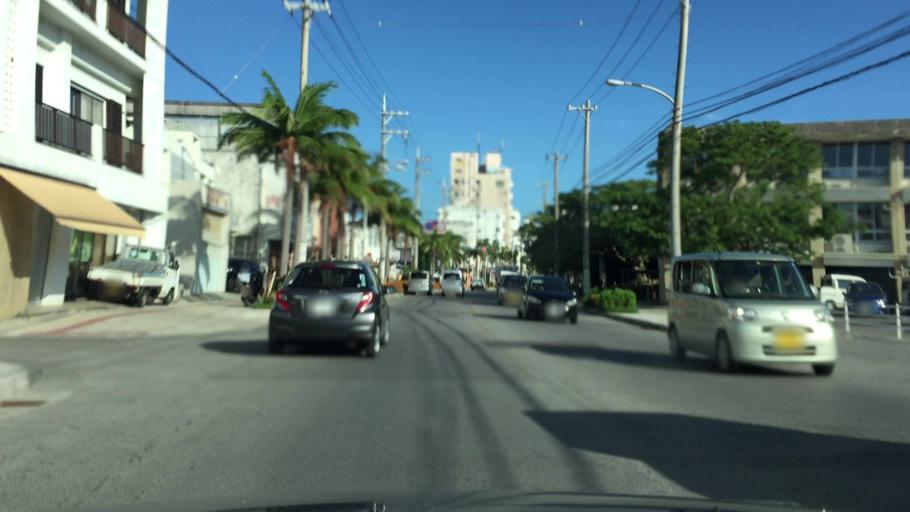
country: JP
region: Okinawa
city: Ishigaki
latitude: 24.3414
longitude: 124.1556
